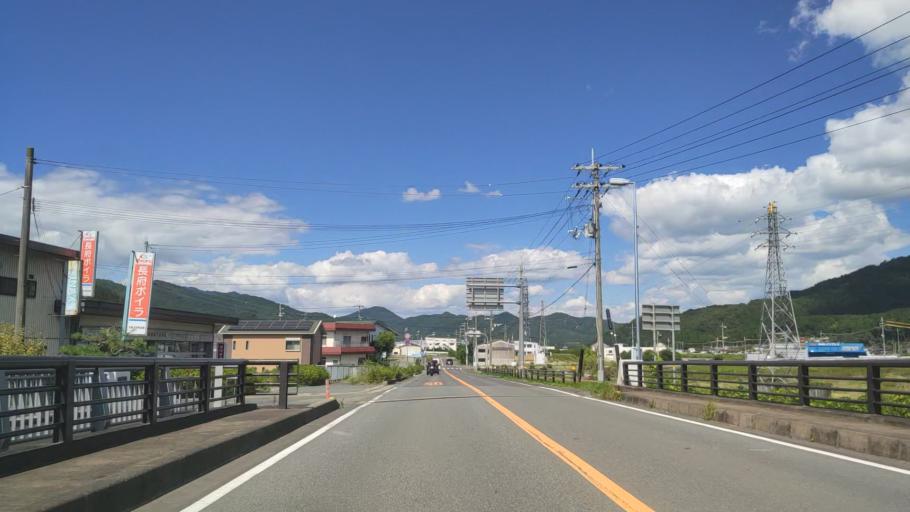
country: JP
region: Kyoto
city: Fukuchiyama
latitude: 35.2125
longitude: 135.1362
